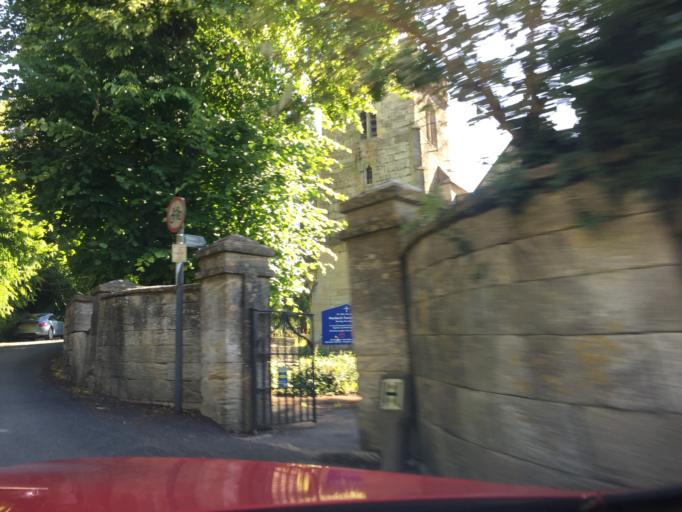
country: GB
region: England
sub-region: Gloucestershire
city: Stonehouse
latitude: 51.7585
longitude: -2.2519
